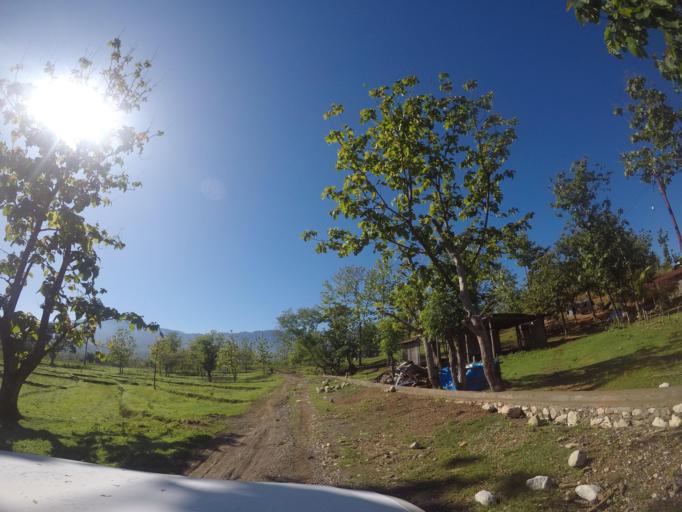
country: TL
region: Bobonaro
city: Maliana
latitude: -8.9960
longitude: 125.1883
